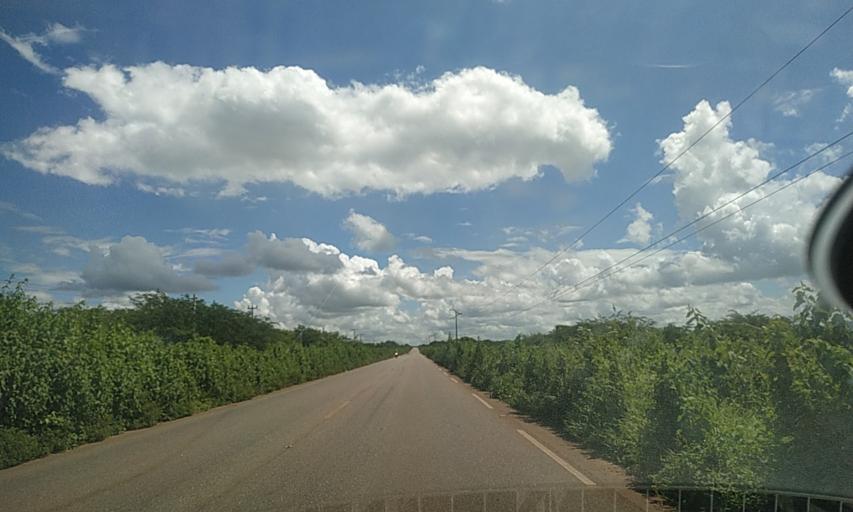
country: BR
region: Rio Grande do Norte
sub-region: Mossoro
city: Mossoro
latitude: -5.1605
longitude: -37.4310
